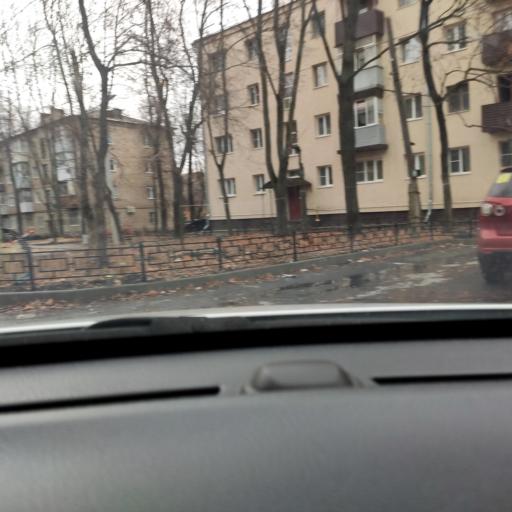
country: RU
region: Voronezj
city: Voronezh
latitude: 51.6780
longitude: 39.1530
